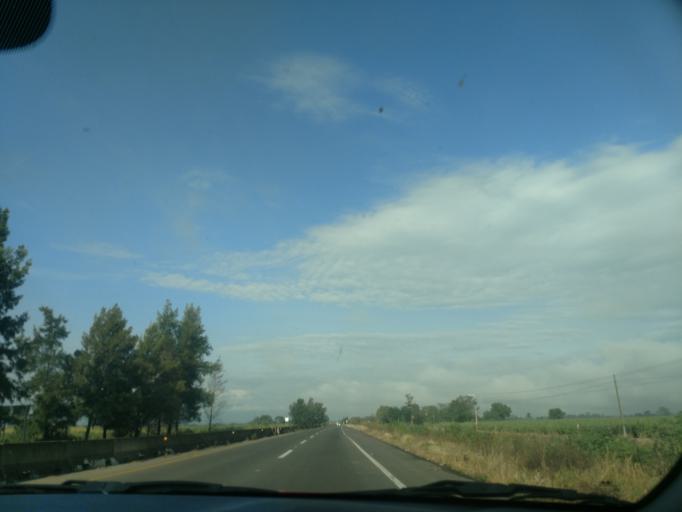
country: MX
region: Jalisco
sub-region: Ameca
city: Los Pocitos
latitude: 20.5340
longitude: -103.9697
